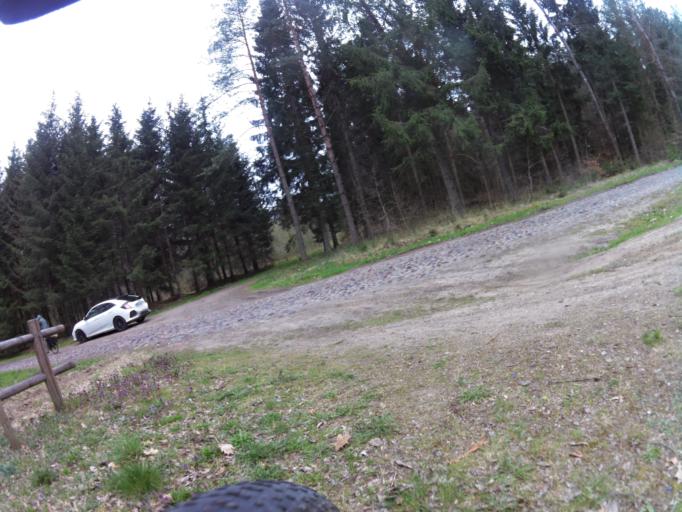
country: PL
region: West Pomeranian Voivodeship
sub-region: Powiat koszalinski
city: Bobolice
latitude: 54.0397
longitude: 16.6167
